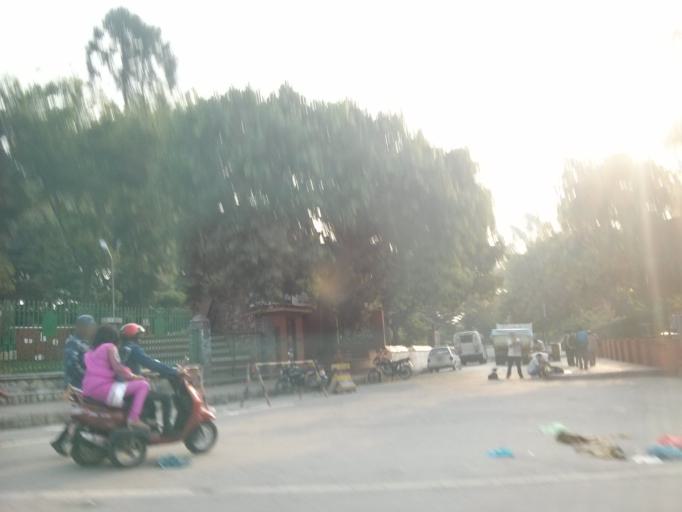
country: NP
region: Central Region
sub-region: Bagmati Zone
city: Kathmandu
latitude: 27.7077
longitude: 85.3438
